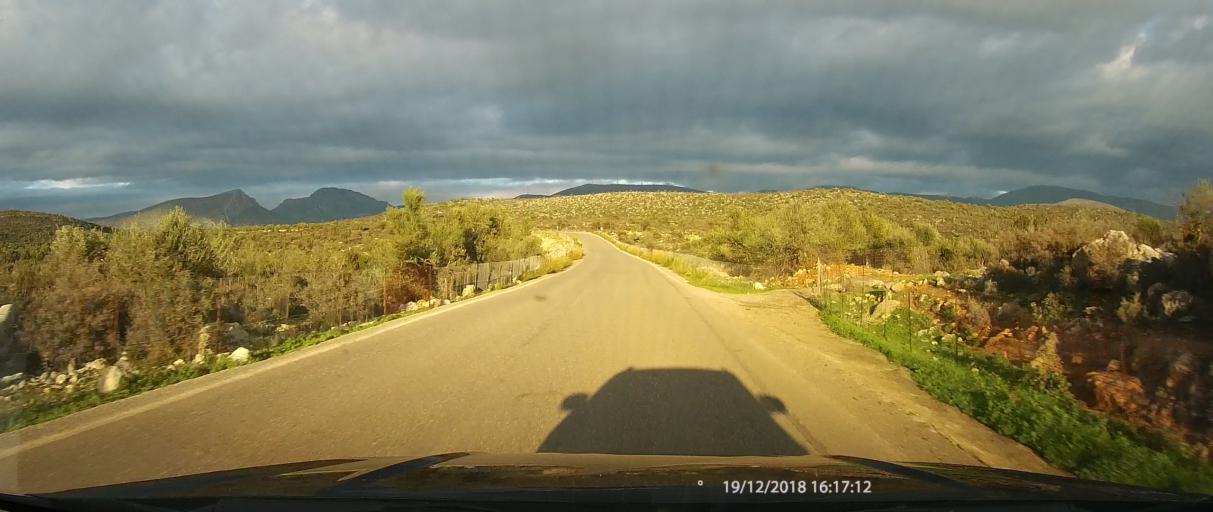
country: GR
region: Peloponnese
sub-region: Nomos Lakonias
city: Kato Glikovrisi
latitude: 36.9081
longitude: 22.8091
